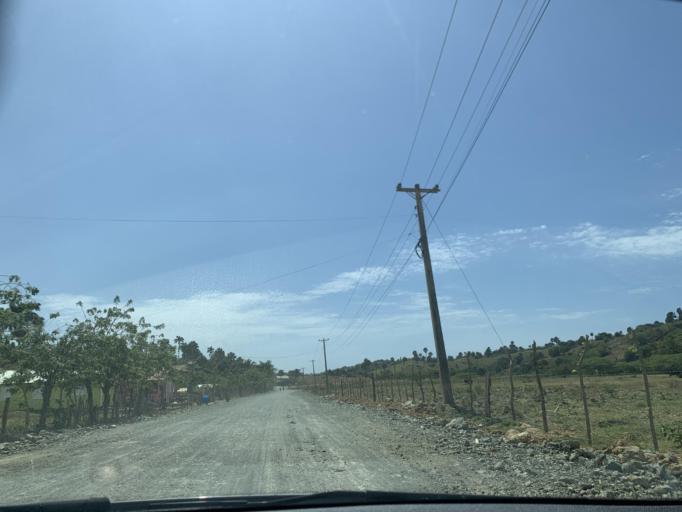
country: DO
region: Puerto Plata
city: Luperon
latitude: 19.8818
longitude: -70.8428
